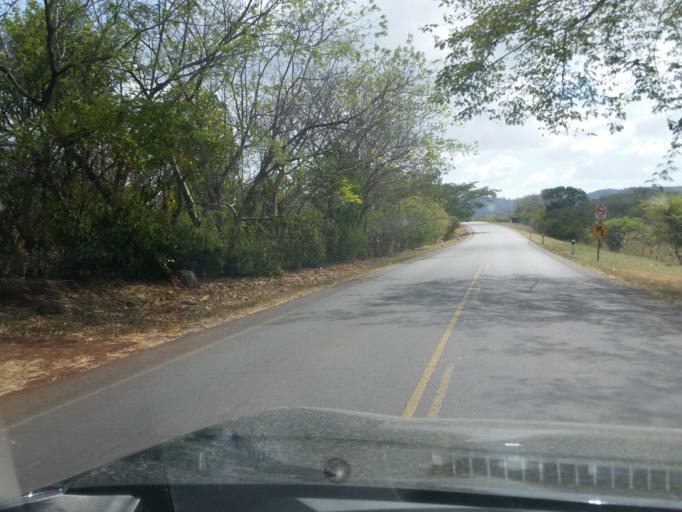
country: NI
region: Chontales
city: Comalapa
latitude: 12.2180
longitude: -85.6378
